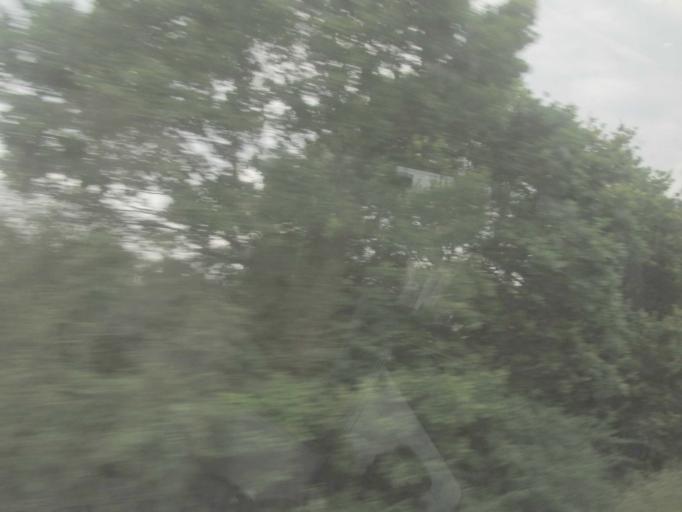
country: GB
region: England
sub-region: Greater London
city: Edgware
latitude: 51.6284
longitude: -0.2642
